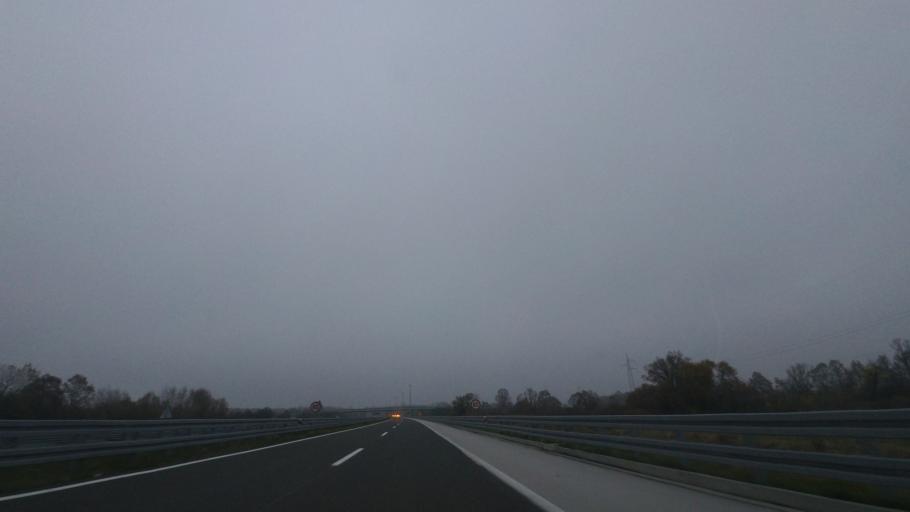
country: HR
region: Sisacko-Moslavacka
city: Lekenik
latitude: 45.5678
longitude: 16.2116
